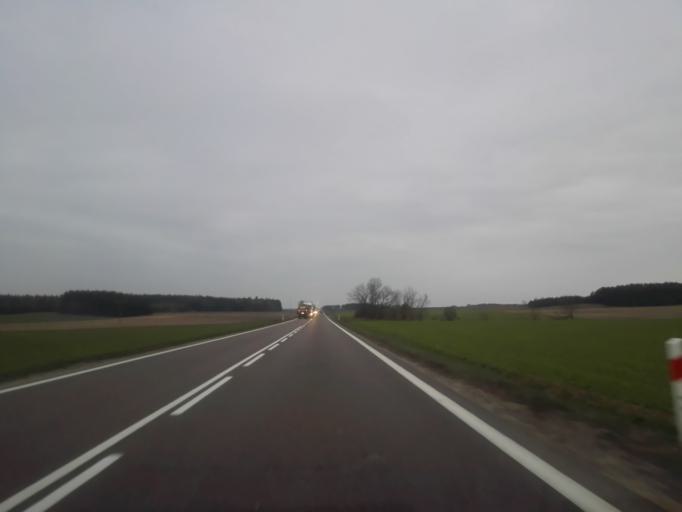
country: PL
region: Podlasie
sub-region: Powiat grajewski
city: Szczuczyn
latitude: 53.4834
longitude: 22.2168
